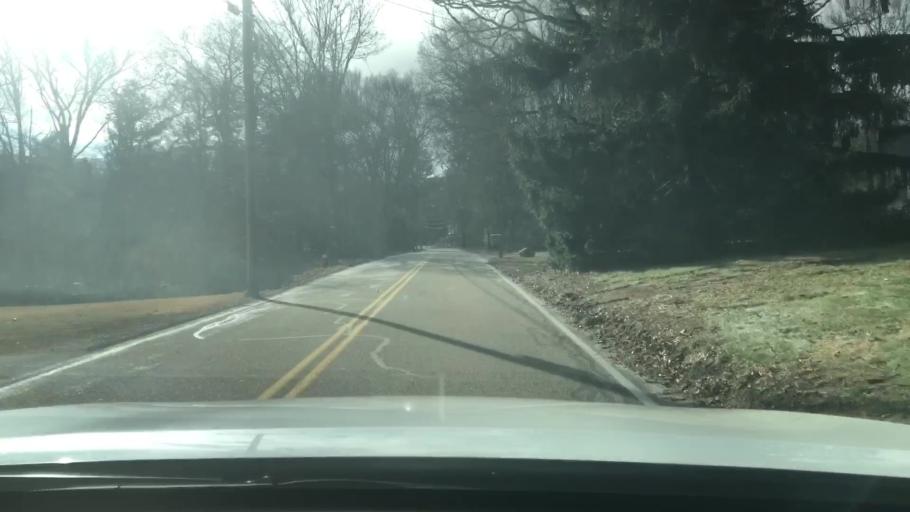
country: US
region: Massachusetts
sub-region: Worcester County
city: Blackstone
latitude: 42.0364
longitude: -71.5240
